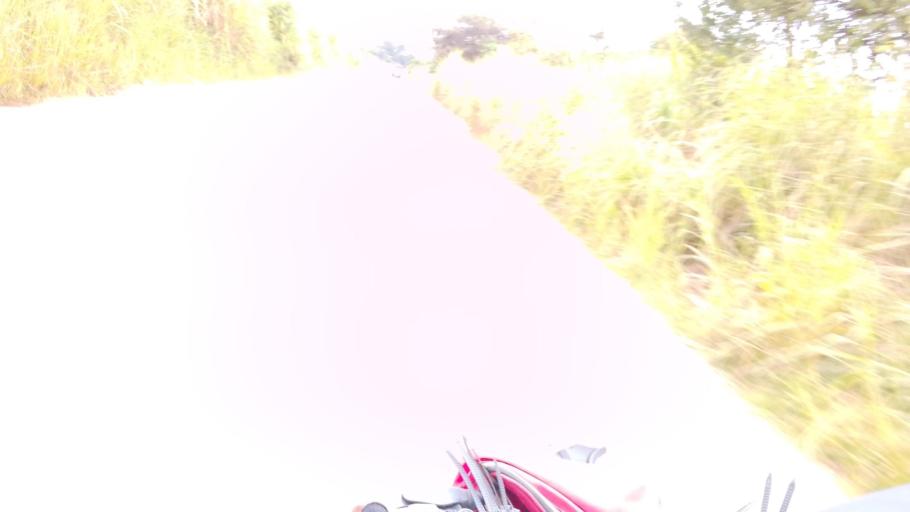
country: SL
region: Eastern Province
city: Koidu
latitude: 8.6734
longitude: -10.9871
